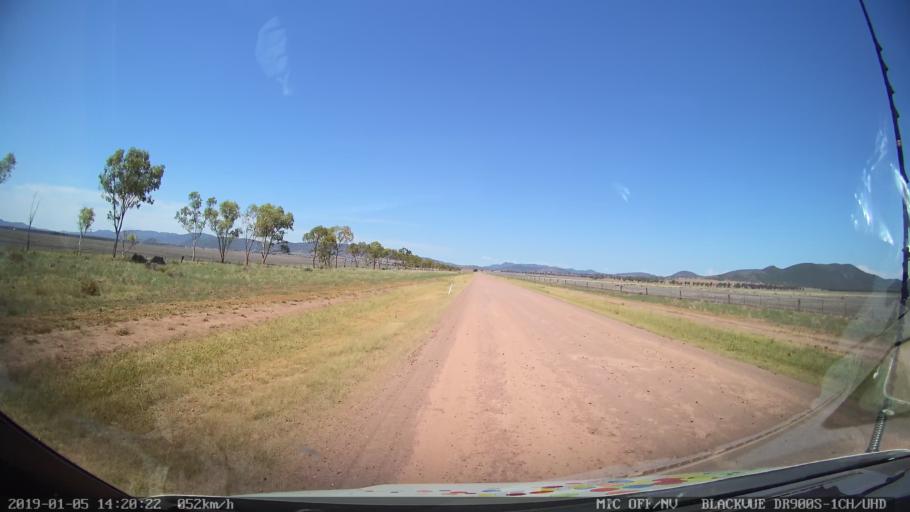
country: AU
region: New South Wales
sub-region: Liverpool Plains
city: Quirindi
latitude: -31.2489
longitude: 150.5041
